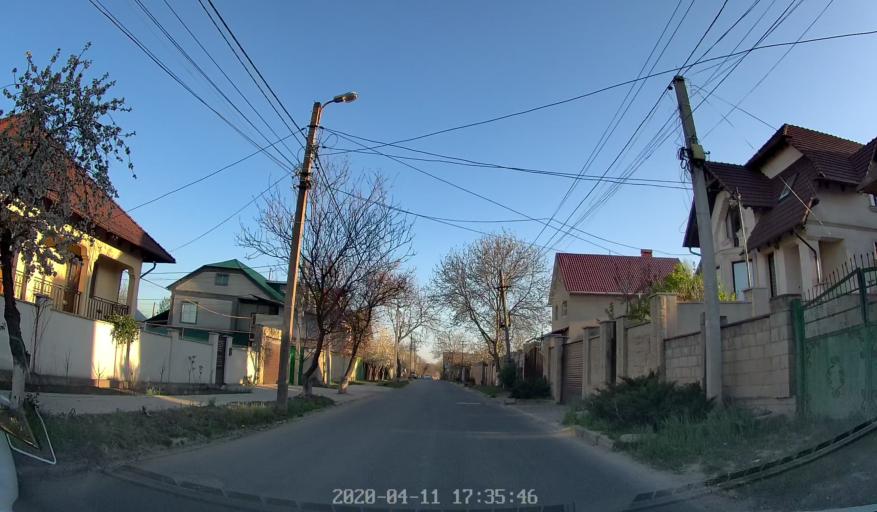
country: MD
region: Laloveni
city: Ialoveni
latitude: 46.9880
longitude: 28.8041
